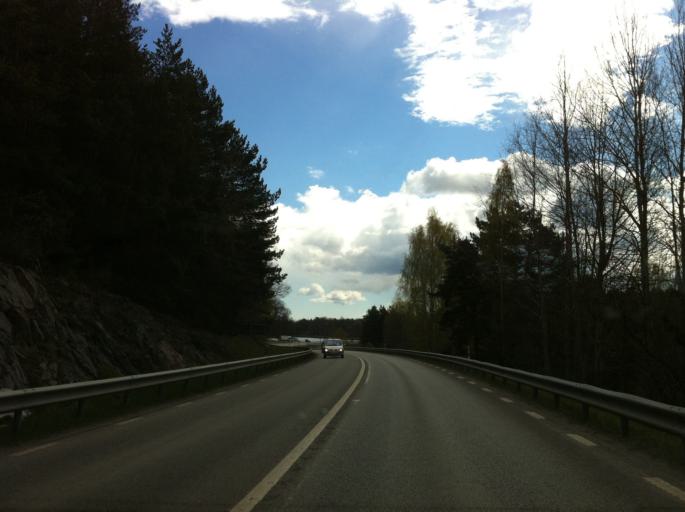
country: SE
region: Stockholm
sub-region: Taby Kommun
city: Taby
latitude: 59.4728
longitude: 18.1601
